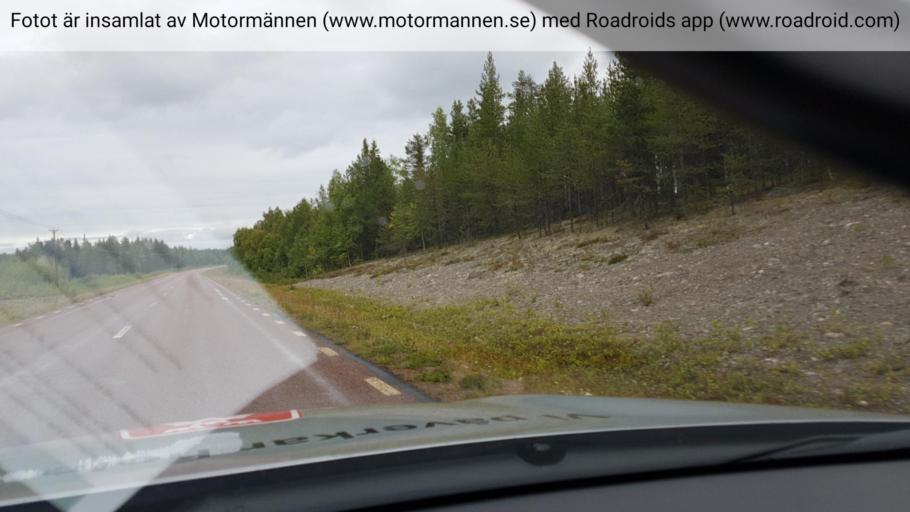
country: SE
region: Norrbotten
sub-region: Pajala Kommun
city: Pajala
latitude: 67.1270
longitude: 22.6065
